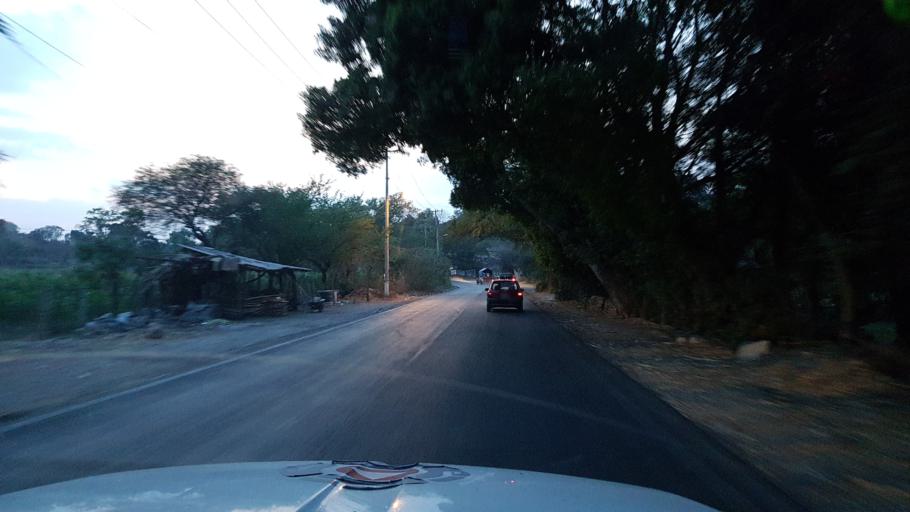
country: MX
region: Morelos
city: Tlaltizapan
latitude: 18.6910
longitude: -99.1301
